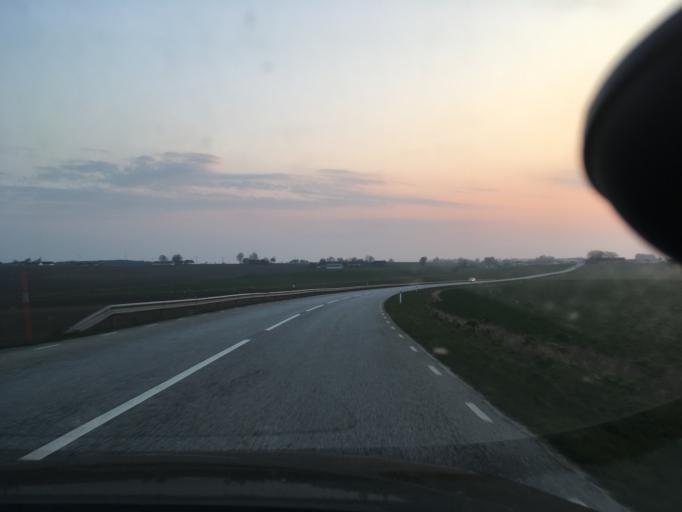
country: SE
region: Skane
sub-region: Tomelilla Kommun
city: Tomelilla
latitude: 55.4748
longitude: 14.0549
